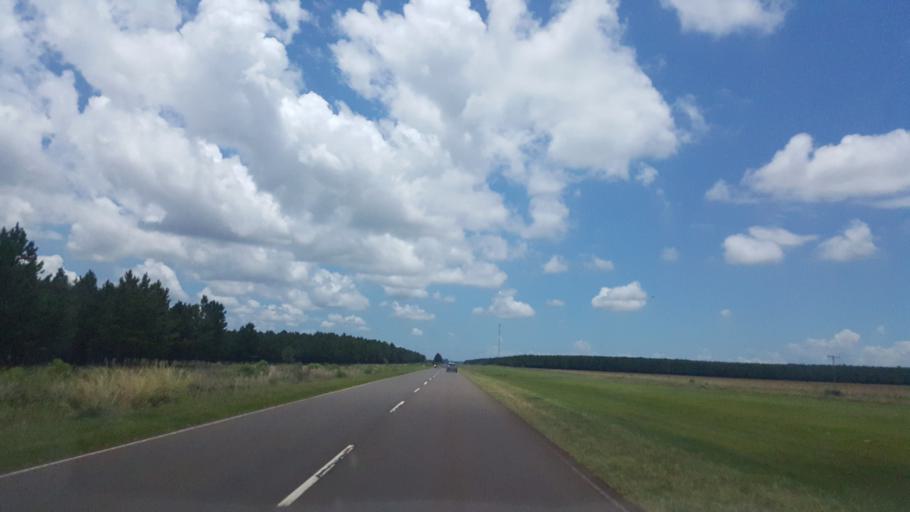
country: PY
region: Itapua
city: San Juan del Parana
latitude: -27.5143
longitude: -56.1439
